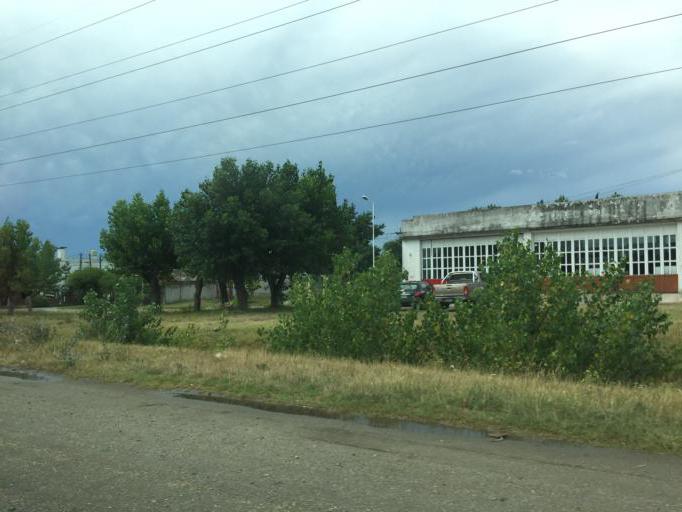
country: AR
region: Buenos Aires
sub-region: Partido de Tandil
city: Tandil
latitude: -37.3093
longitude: -59.1170
